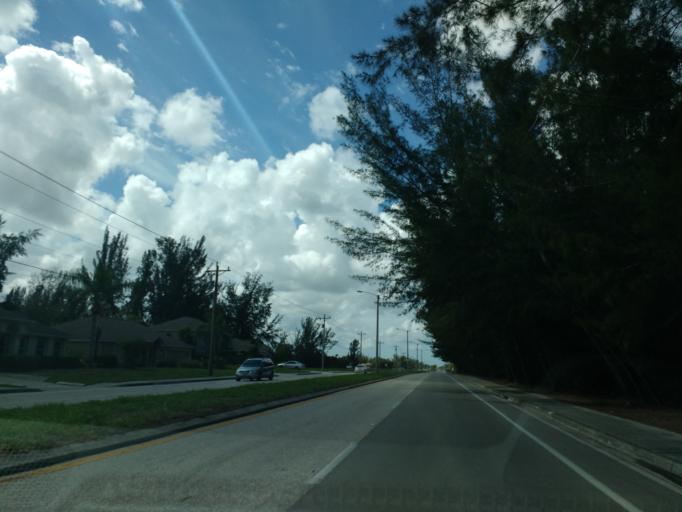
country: US
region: Florida
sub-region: Lee County
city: Cape Coral
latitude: 26.6325
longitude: -82.0072
